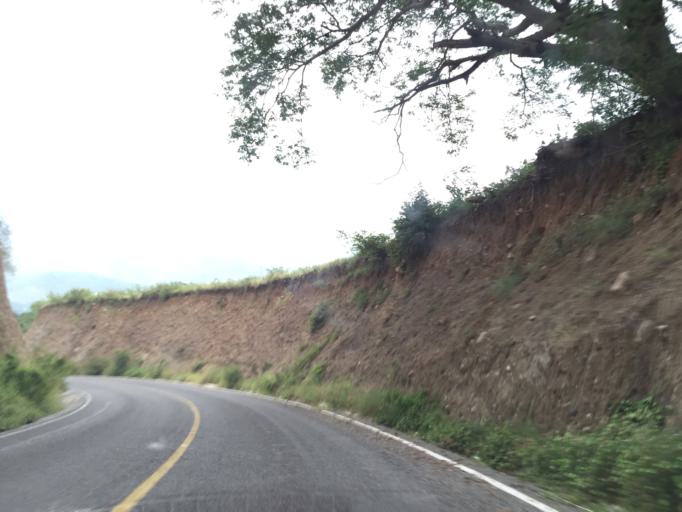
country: MX
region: Colima
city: Comala
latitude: 19.3670
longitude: -103.7985
